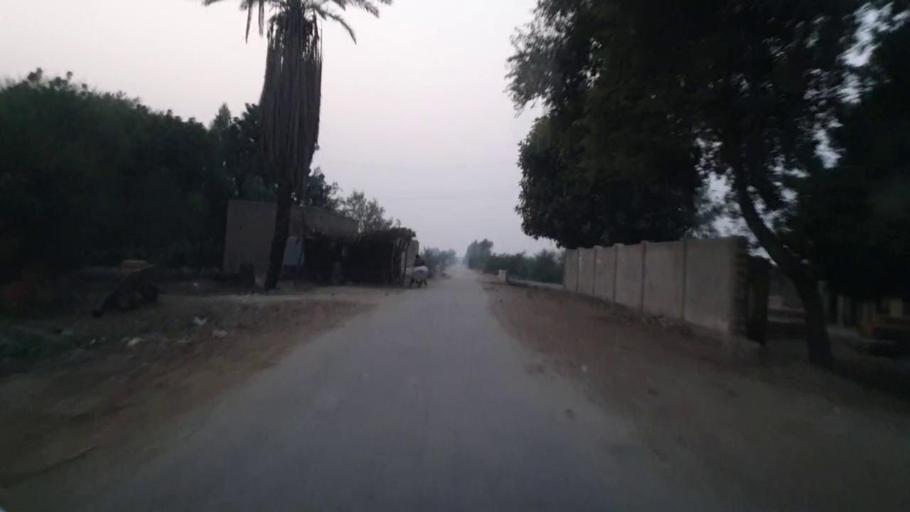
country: PK
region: Sindh
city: Karaundi
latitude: 26.9229
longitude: 68.4222
